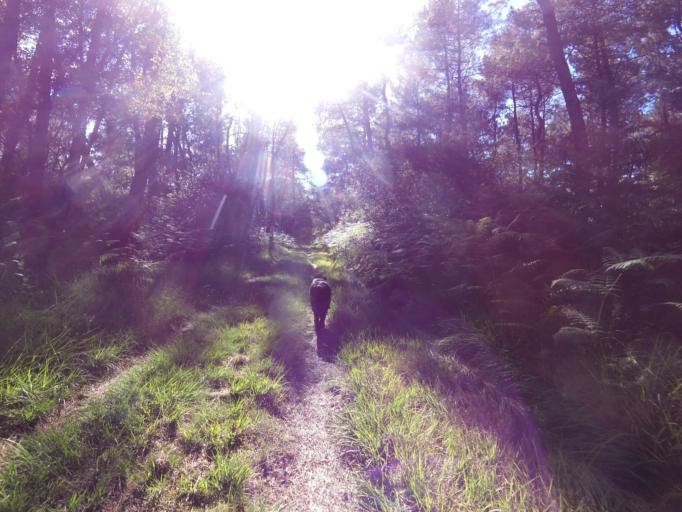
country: FR
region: Brittany
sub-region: Departement du Morbihan
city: Pleucadeuc
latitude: 47.7543
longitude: -2.4074
